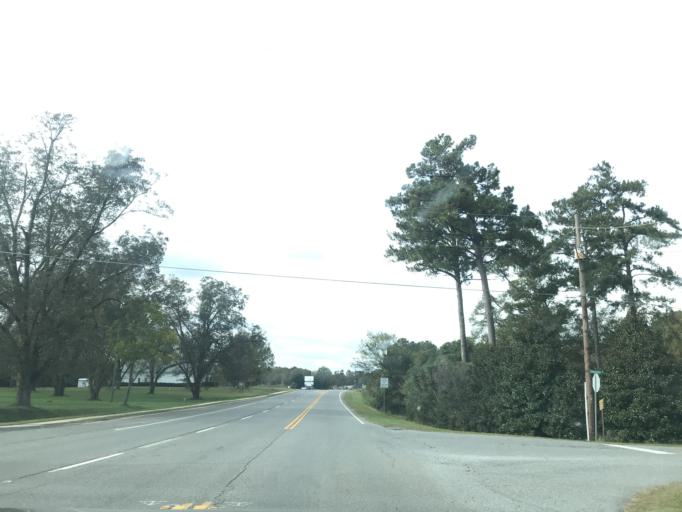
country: US
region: Georgia
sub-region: Jones County
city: Gray
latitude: 32.9981
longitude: -83.5281
